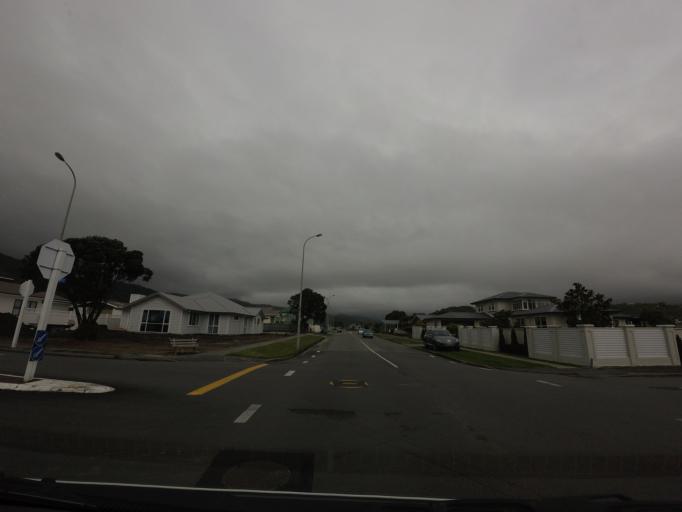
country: NZ
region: West Coast
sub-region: Grey District
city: Greymouth
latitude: -42.4605
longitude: 171.1976
